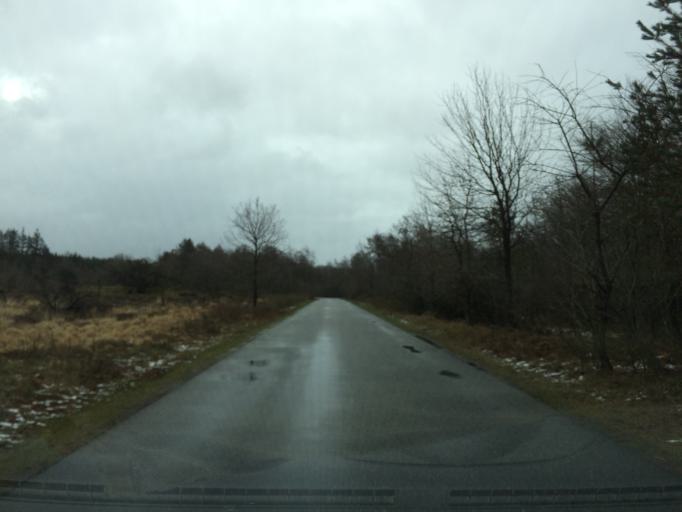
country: DK
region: Central Jutland
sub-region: Ringkobing-Skjern Kommune
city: Videbaek
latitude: 56.2096
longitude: 8.5415
